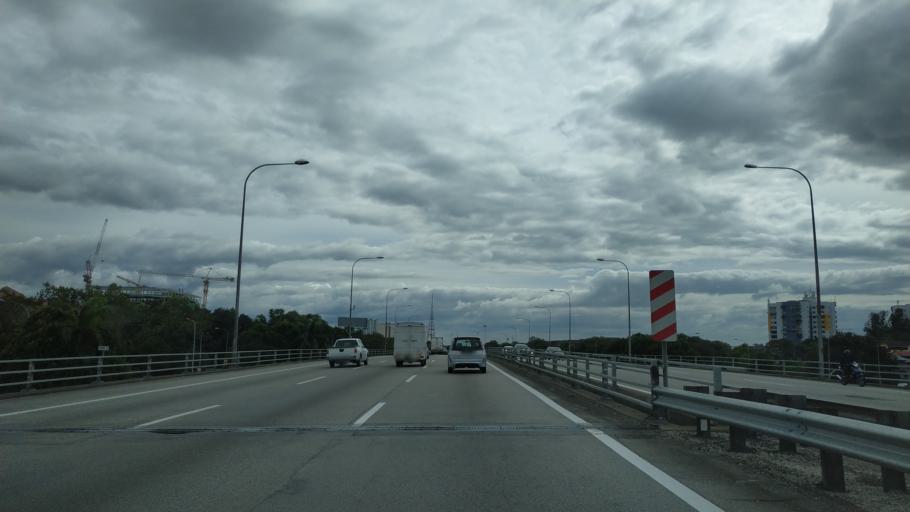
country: MY
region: Penang
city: Perai
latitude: 5.4001
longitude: 100.4066
